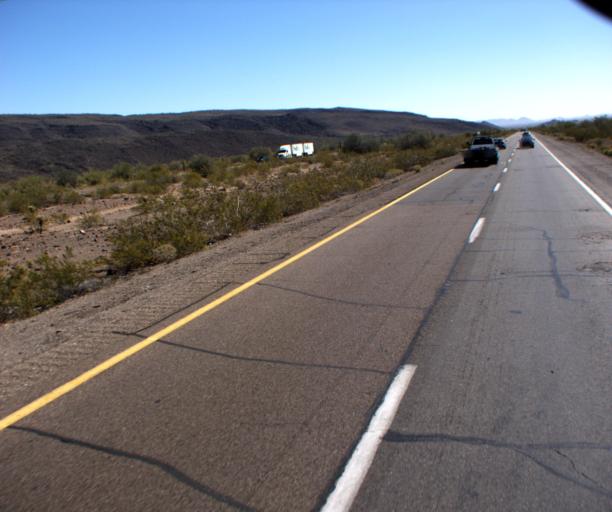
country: US
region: Arizona
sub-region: La Paz County
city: Quartzsite
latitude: 33.6514
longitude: -113.9274
